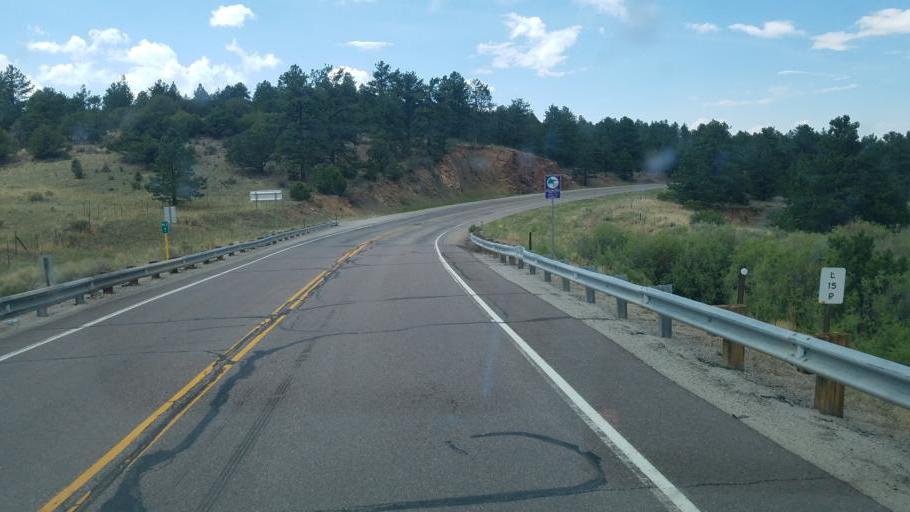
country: US
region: Colorado
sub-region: Custer County
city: Westcliffe
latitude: 38.1440
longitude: -105.3505
